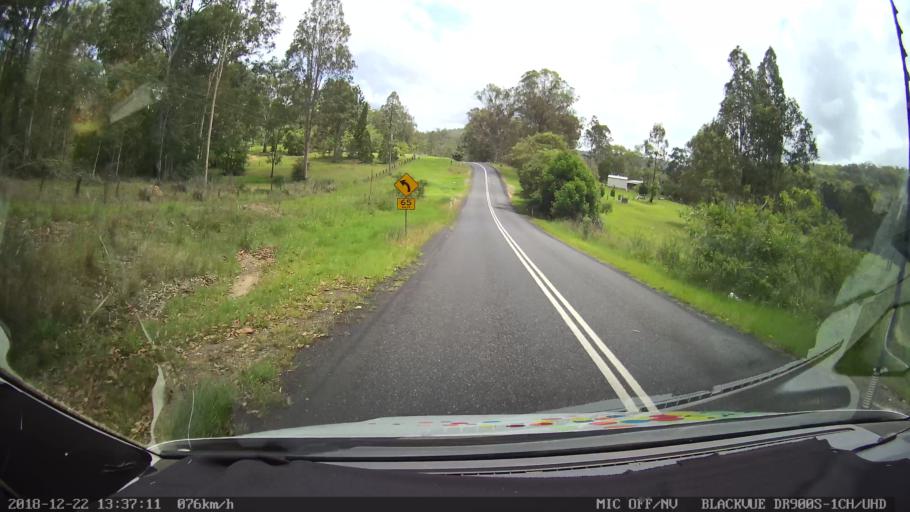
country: AU
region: New South Wales
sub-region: Clarence Valley
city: Coutts Crossing
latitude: -29.8874
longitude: 152.7889
